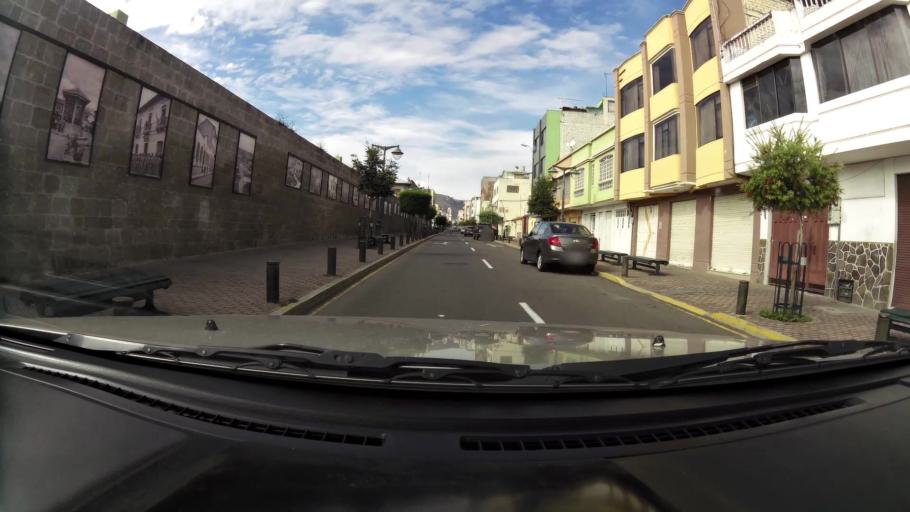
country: EC
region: Tungurahua
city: Ambato
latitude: -1.2358
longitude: -78.6234
